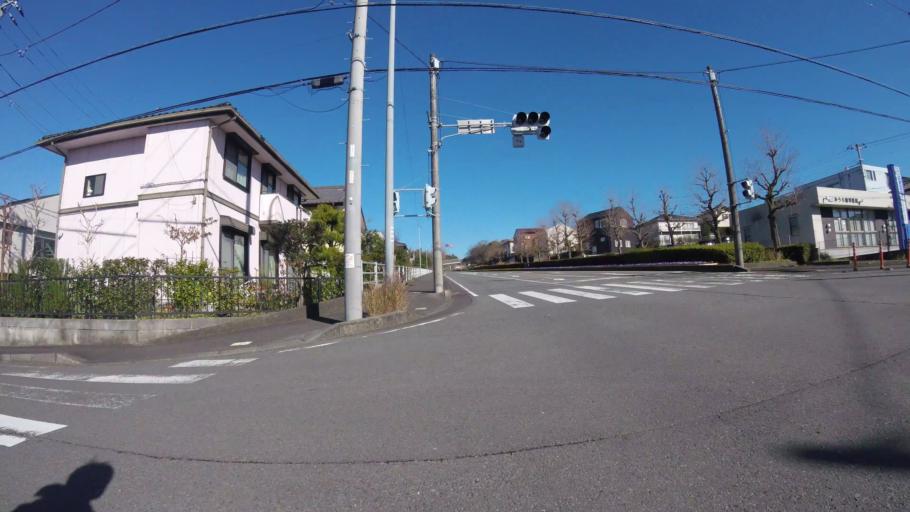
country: JP
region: Shizuoka
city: Mishima
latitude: 35.1270
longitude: 138.9339
